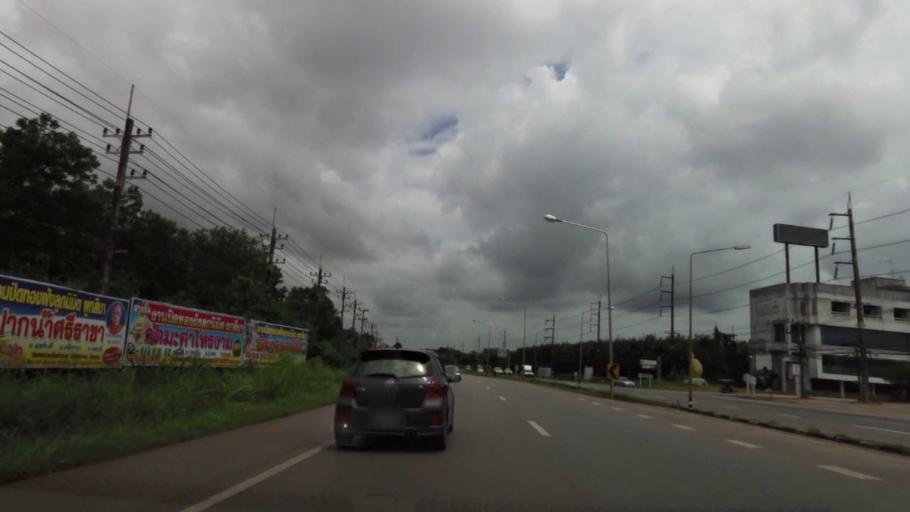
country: TH
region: Chanthaburi
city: Na Yai Am
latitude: 12.7666
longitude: 101.8504
